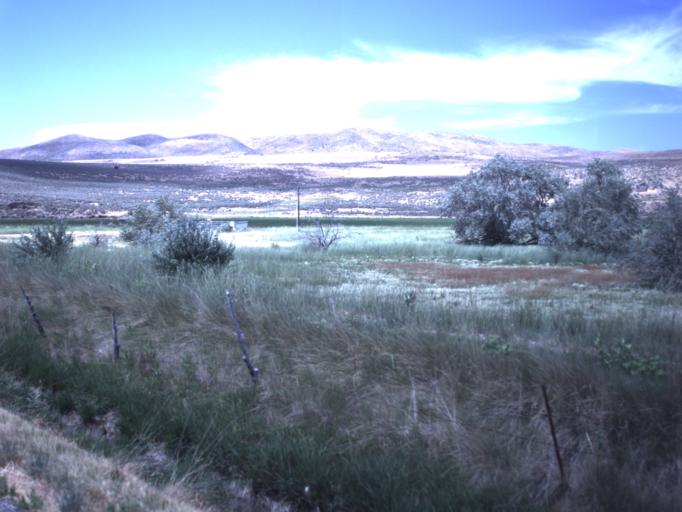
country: US
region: Utah
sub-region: Box Elder County
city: Tremonton
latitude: 41.6369
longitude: -112.3244
